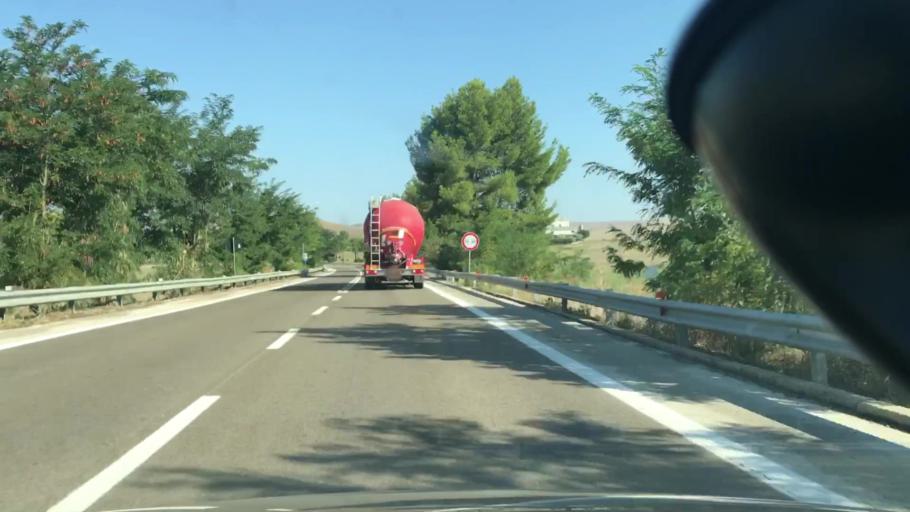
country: IT
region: Basilicate
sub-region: Provincia di Matera
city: Irsina
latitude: 40.8034
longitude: 16.2739
